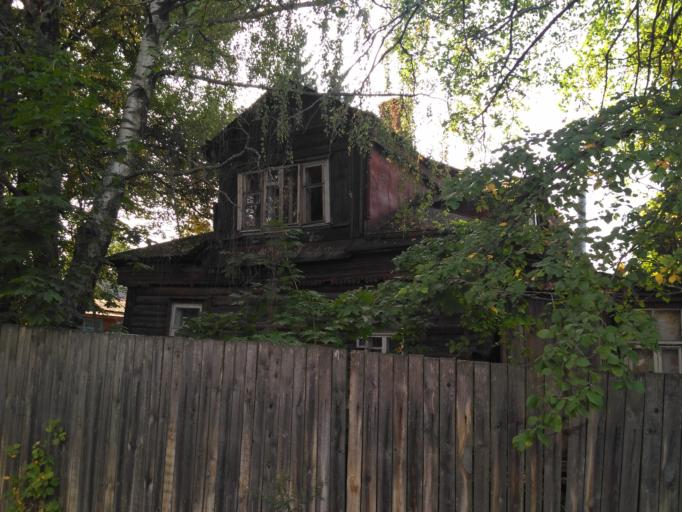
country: RU
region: Moskovskaya
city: Sergiyev Posad
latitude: 56.3097
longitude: 38.1549
